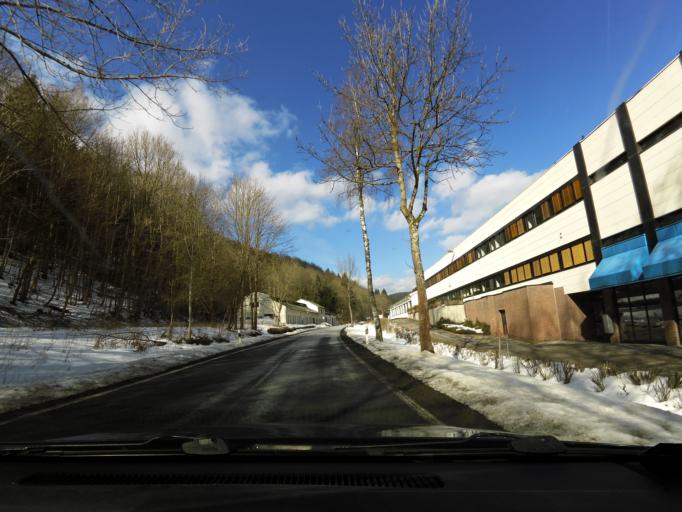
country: DE
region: Lower Saxony
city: Sankt Andreasberg
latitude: 51.6748
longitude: 10.5012
